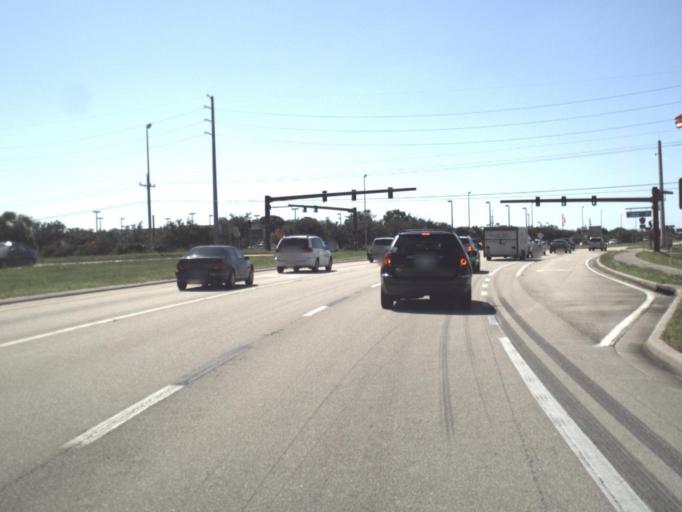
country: US
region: Florida
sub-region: Charlotte County
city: Rotonda
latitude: 26.9338
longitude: -82.2210
